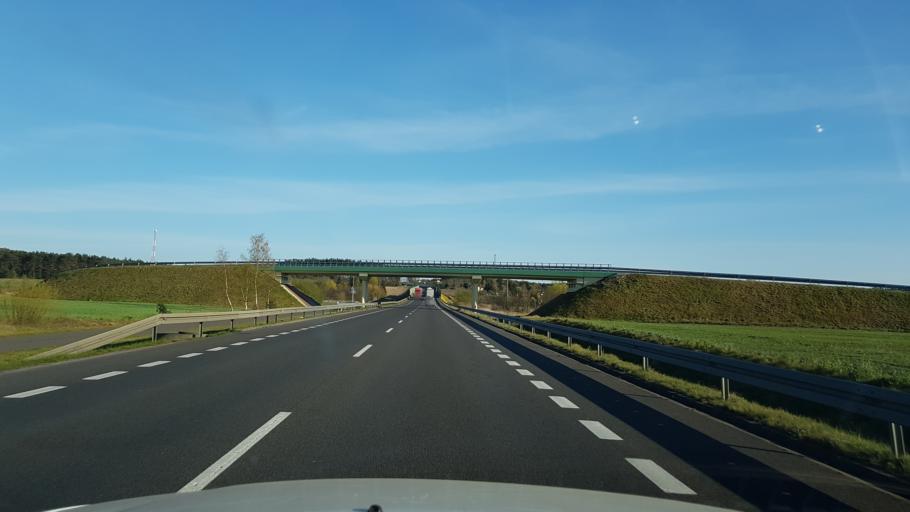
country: PL
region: West Pomeranian Voivodeship
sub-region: Powiat kamienski
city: Wolin
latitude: 53.8757
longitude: 14.5363
